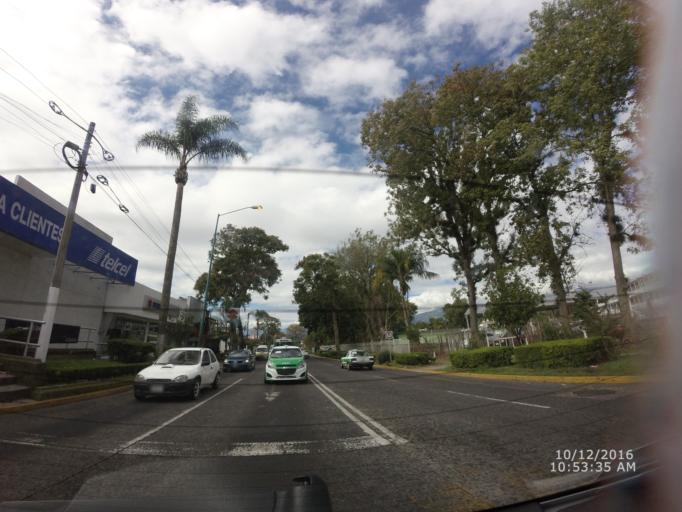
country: MX
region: Veracruz
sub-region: Xalapa
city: Xalapa de Enriquez
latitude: 19.5402
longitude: -96.9265
